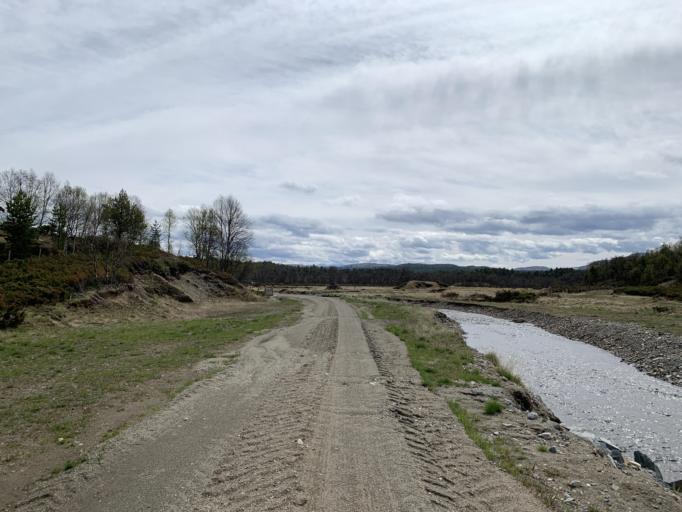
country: NO
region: Hedmark
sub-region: Alvdal
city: Alvdal
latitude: 62.4123
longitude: 10.3994
